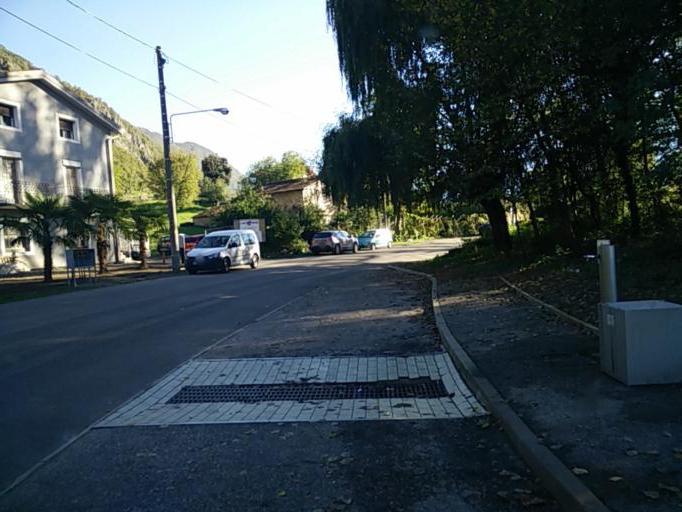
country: IT
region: Trentino-Alto Adige
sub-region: Bolzano
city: Sinigo
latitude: 46.6230
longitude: 11.1867
